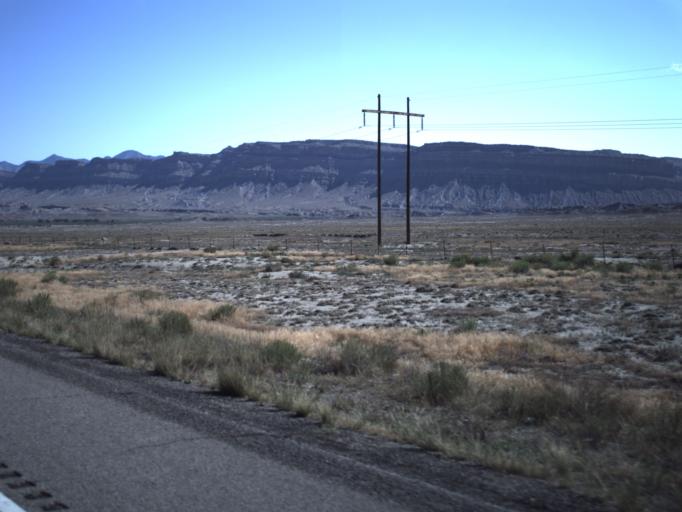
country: US
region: Utah
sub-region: Carbon County
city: East Carbon City
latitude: 39.2266
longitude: -110.3387
